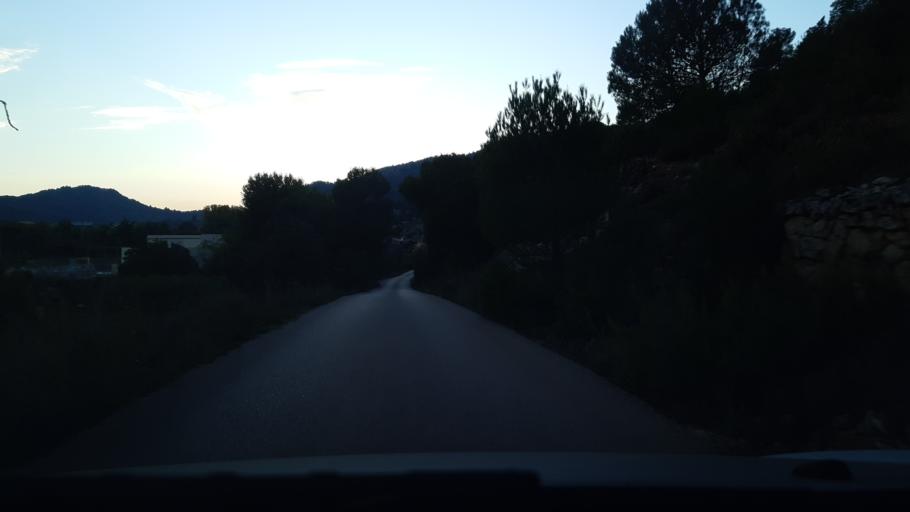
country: ES
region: Aragon
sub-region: Provincia de Teruel
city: Valderrobres
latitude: 40.8397
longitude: 0.1905
